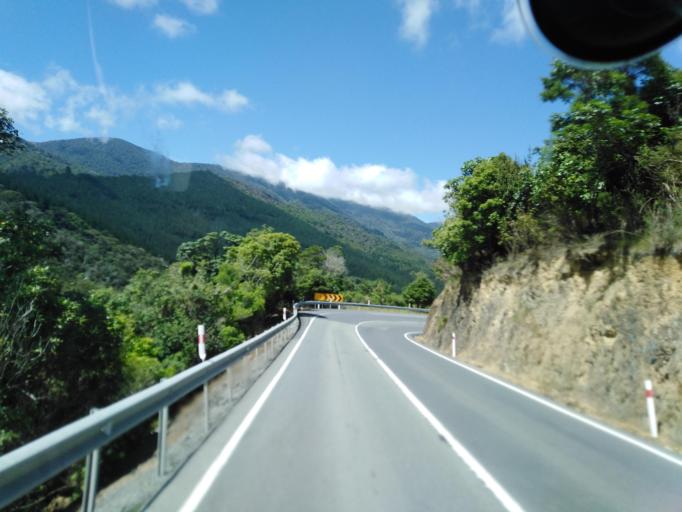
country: NZ
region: Nelson
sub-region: Nelson City
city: Nelson
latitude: -41.2283
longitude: 173.4360
